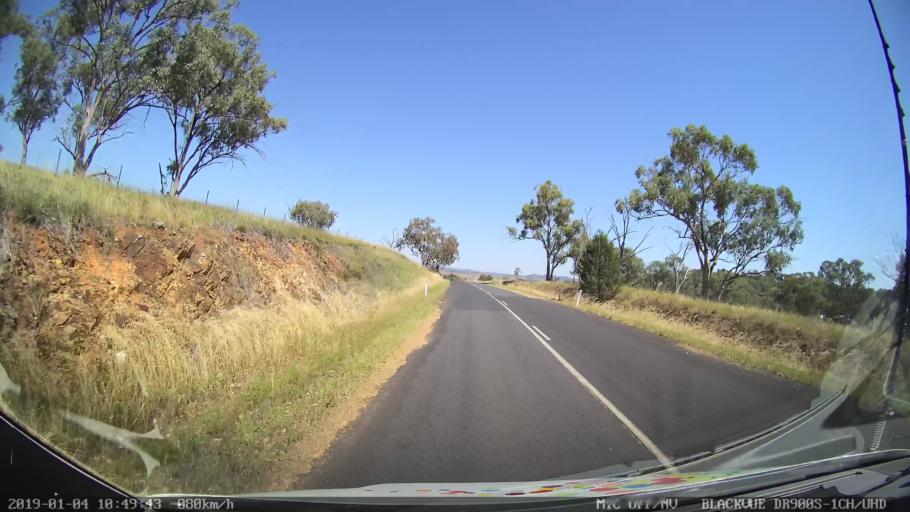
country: AU
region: New South Wales
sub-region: Cabonne
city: Molong
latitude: -33.2460
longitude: 148.7036
